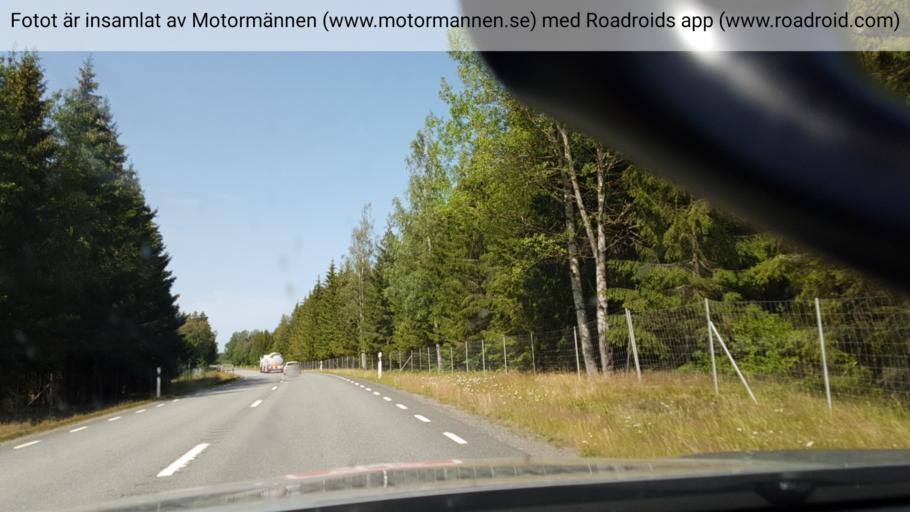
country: SE
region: Joenkoeping
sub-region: Eksjo Kommun
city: Eksjoe
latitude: 57.6984
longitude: 14.9524
